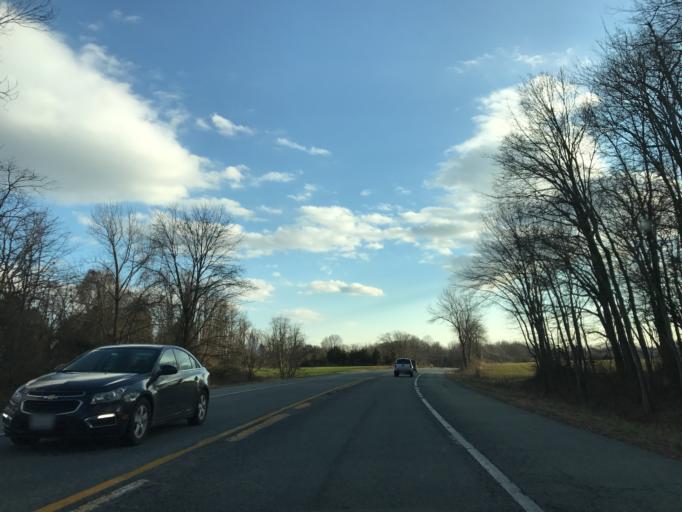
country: US
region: Maryland
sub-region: Cecil County
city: North East
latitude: 39.6546
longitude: -75.9528
